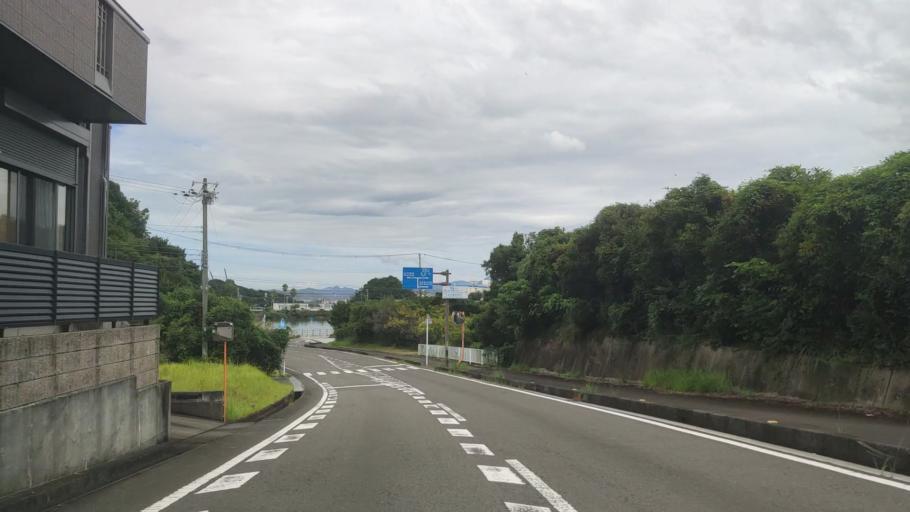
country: JP
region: Wakayama
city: Tanabe
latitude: 33.6900
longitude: 135.3881
